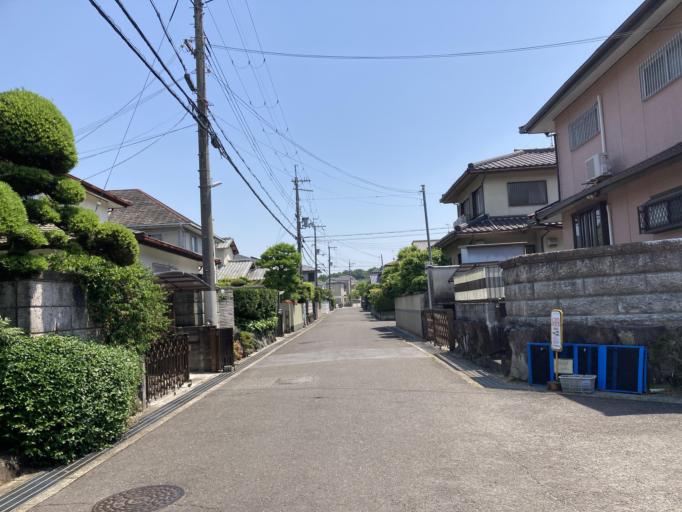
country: JP
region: Nara
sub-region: Ikoma-shi
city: Ikoma
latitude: 34.7101
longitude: 135.7212
